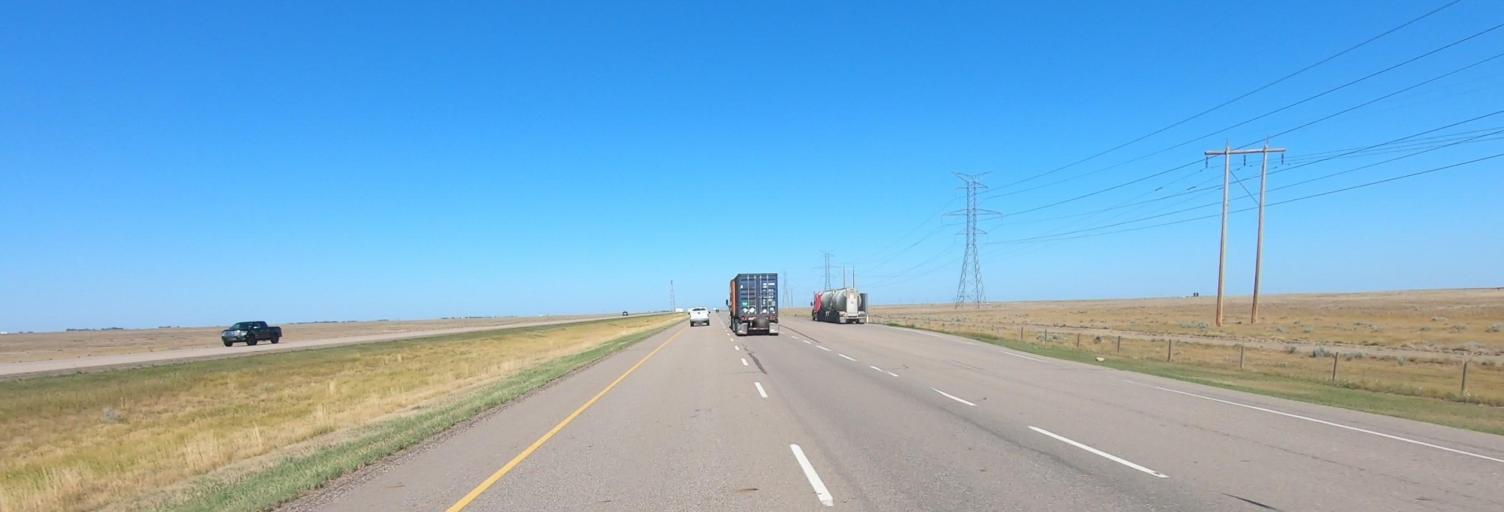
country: CA
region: Alberta
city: Brooks
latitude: 50.4308
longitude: -111.5401
